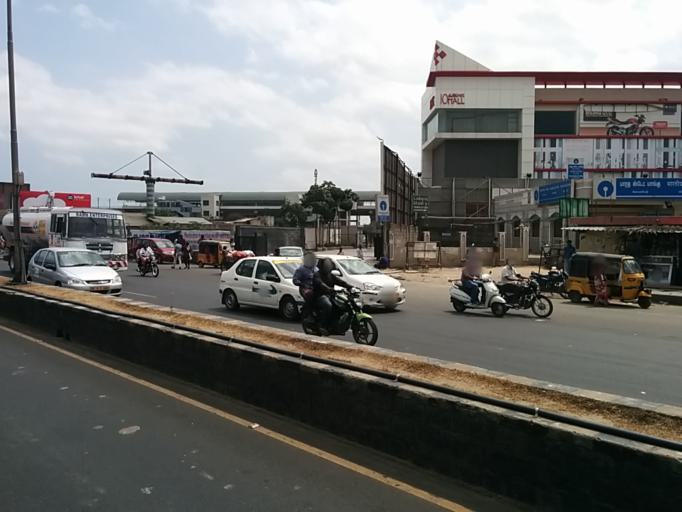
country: IN
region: Tamil Nadu
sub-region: Chennai
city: Chetput
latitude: 13.0712
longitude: 80.2034
